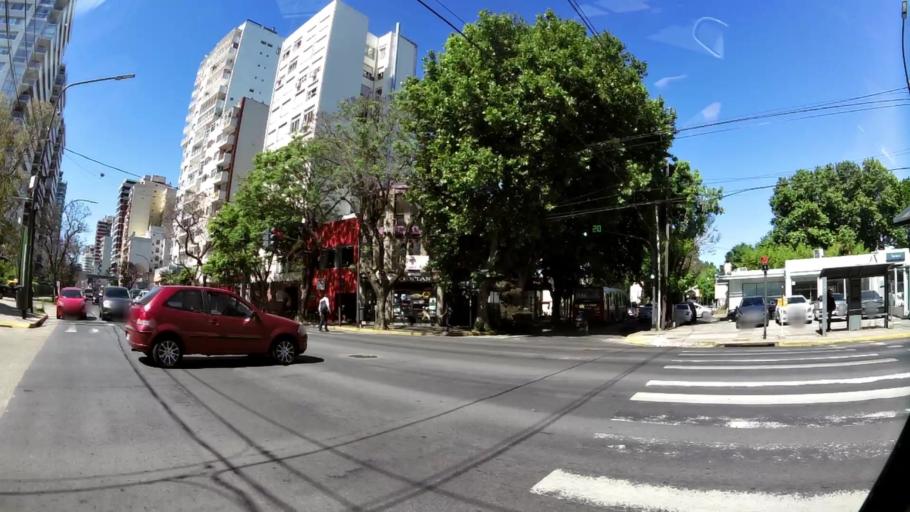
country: AR
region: Buenos Aires
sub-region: Partido de Vicente Lopez
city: Olivos
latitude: -34.5165
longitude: -58.4760
